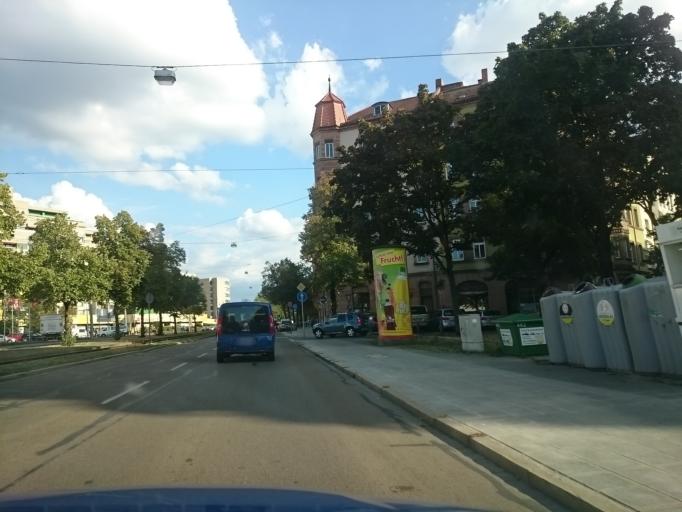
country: DE
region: Bavaria
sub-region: Regierungsbezirk Mittelfranken
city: Nuernberg
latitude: 49.4418
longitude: 11.1010
